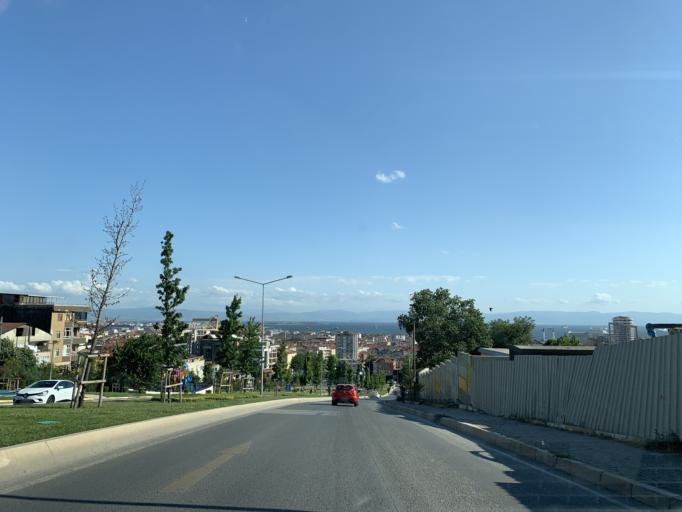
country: TR
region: Istanbul
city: Pendik
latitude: 40.8832
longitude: 29.2595
